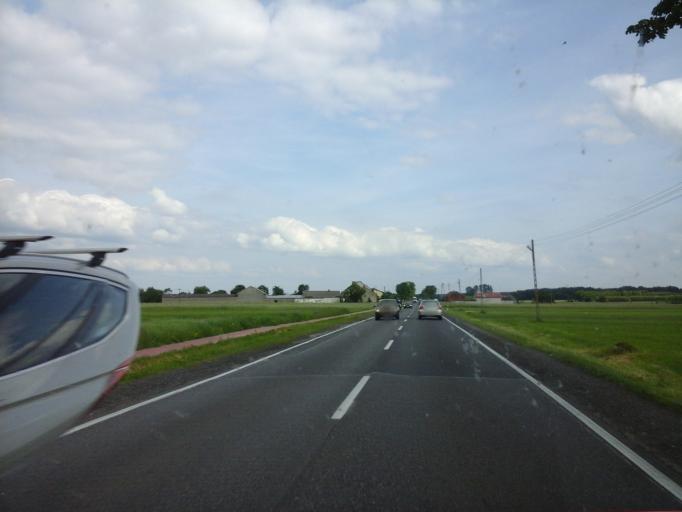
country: PL
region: Lodz Voivodeship
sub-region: Powiat opoczynski
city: Mniszkow
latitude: 51.3246
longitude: 20.0439
